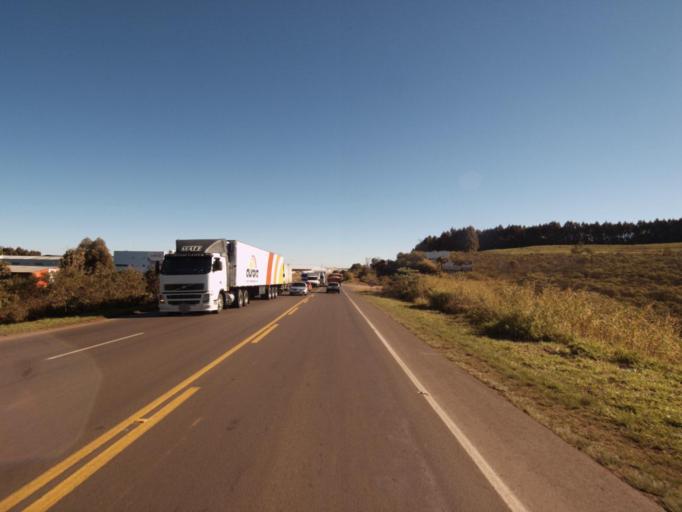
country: BR
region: Santa Catarina
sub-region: Chapeco
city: Chapeco
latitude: -26.9649
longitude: -52.5524
